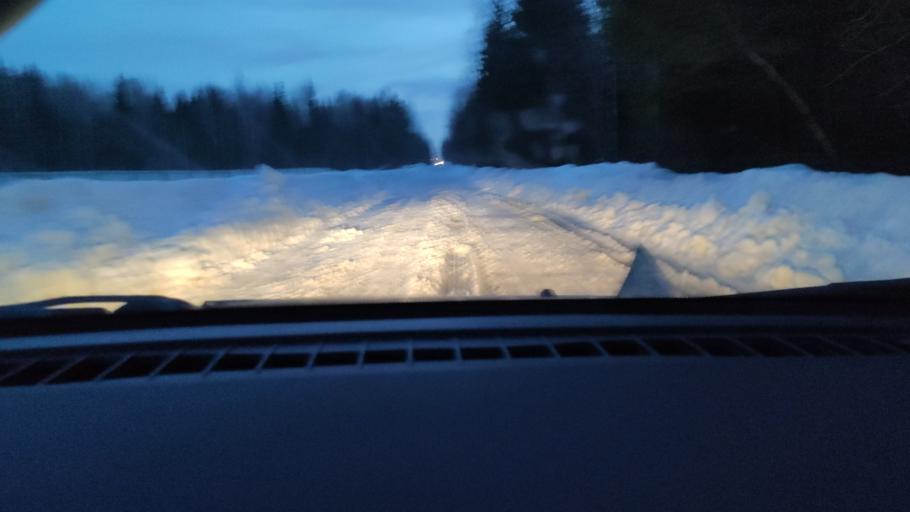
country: RU
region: Perm
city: Kondratovo
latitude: 58.0706
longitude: 56.1277
